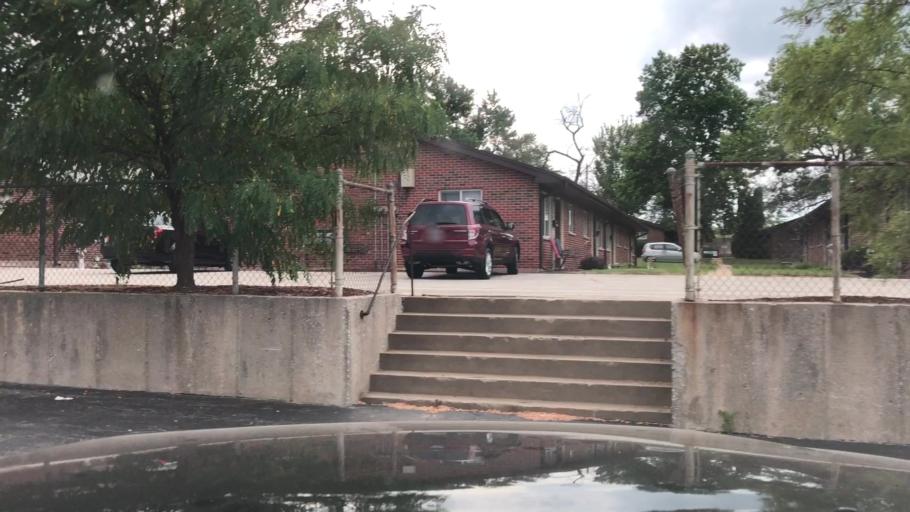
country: US
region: Missouri
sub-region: Saint Charles County
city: Saint Charles
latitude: 38.7851
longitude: -90.5129
